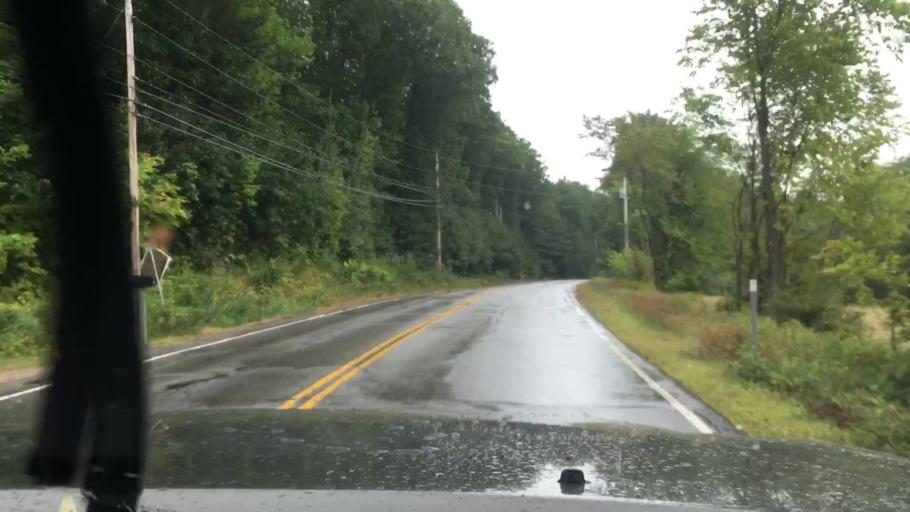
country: US
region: New Hampshire
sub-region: Belknap County
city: Meredith
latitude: 43.6501
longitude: -71.5433
